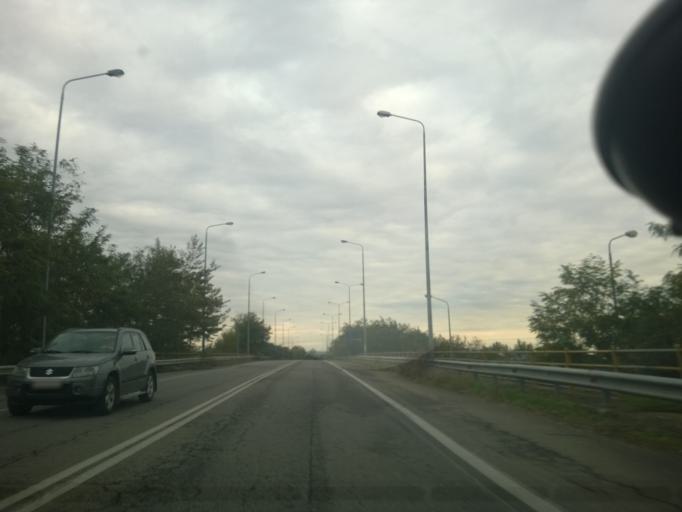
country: GR
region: Central Macedonia
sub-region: Nomos Pellis
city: Melissi
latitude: 40.7778
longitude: 22.3601
